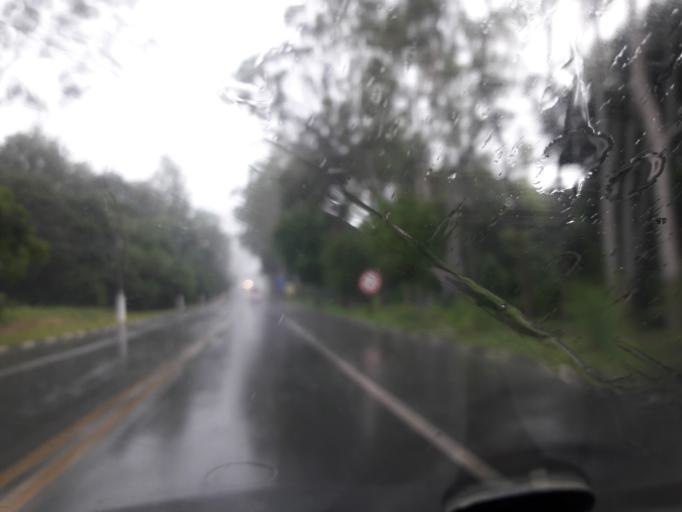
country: BR
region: Sao Paulo
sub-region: Bom Jesus Dos Perdoes
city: Bom Jesus dos Perdoes
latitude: -23.1717
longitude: -46.3948
